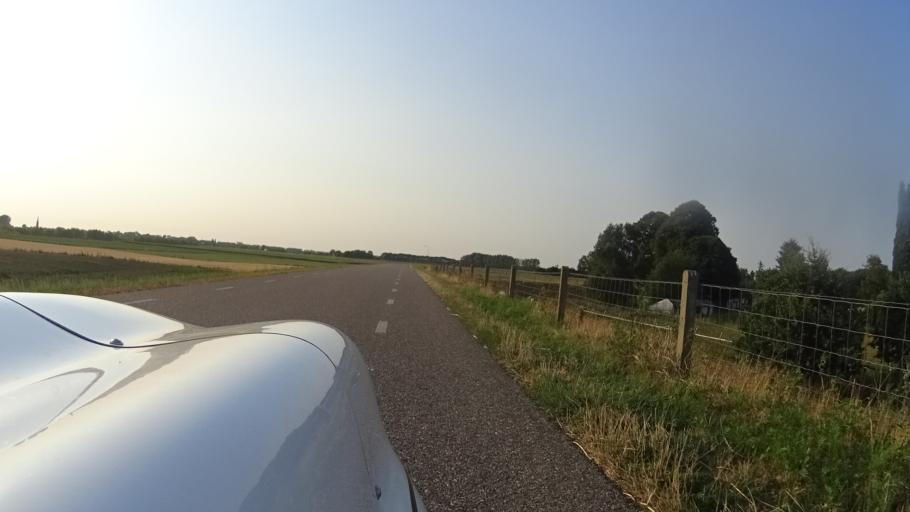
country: NL
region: Gelderland
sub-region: Gemeente Wijchen
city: Bergharen
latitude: 51.8159
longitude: 5.6542
